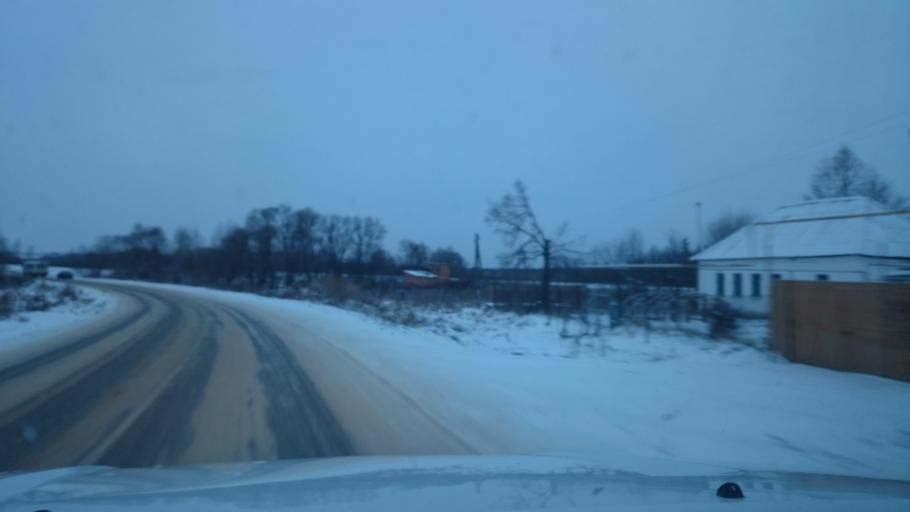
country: RU
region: Tula
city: Leninskiy
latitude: 54.2527
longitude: 37.3688
